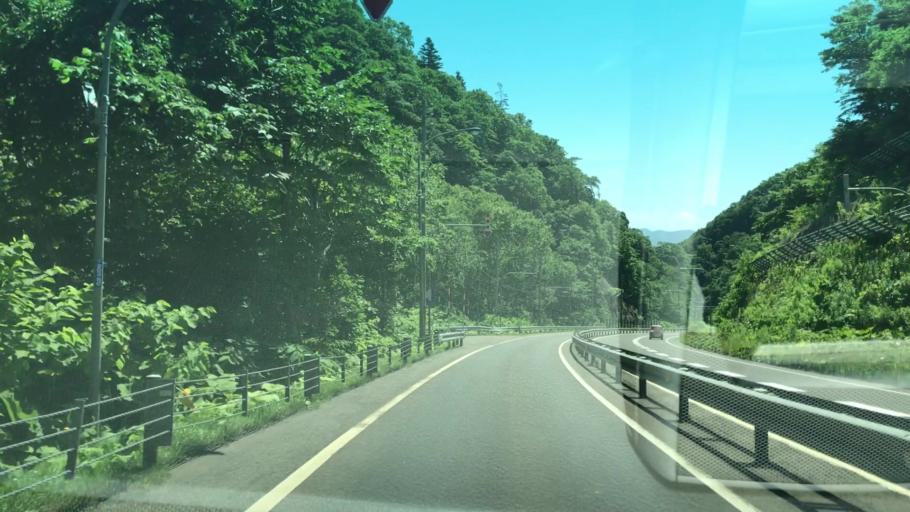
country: JP
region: Hokkaido
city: Yoichi
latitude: 43.0441
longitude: 140.6814
